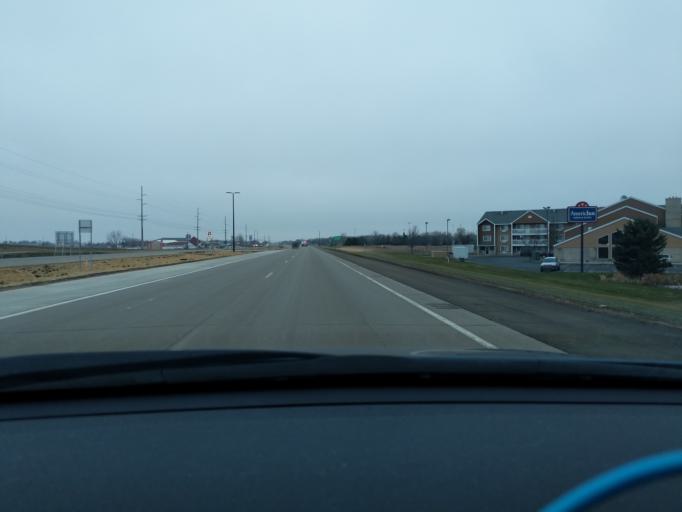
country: US
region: Minnesota
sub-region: Lyon County
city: Marshall
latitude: 44.4431
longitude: -95.7620
